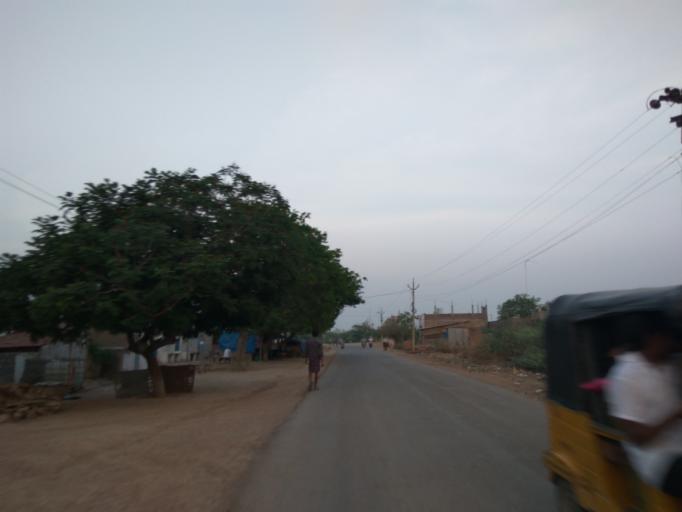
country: IN
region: Andhra Pradesh
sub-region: Prakasam
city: Markapur
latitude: 15.7401
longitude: 79.2529
